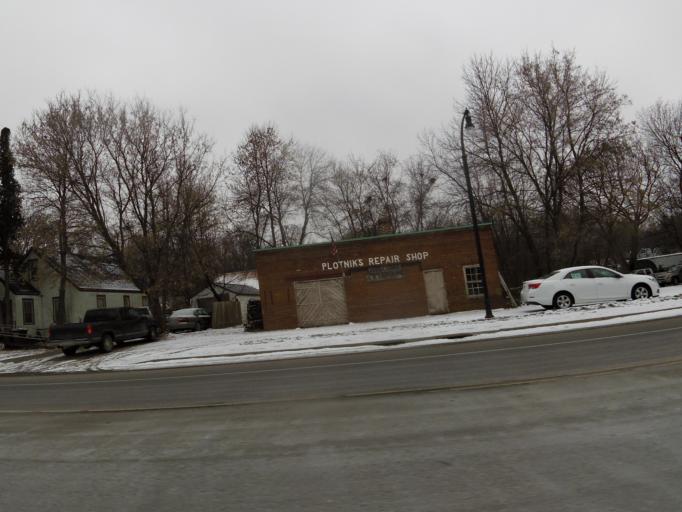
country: US
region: Minnesota
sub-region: Wright County
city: Delano
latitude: 45.0410
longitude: -93.7915
